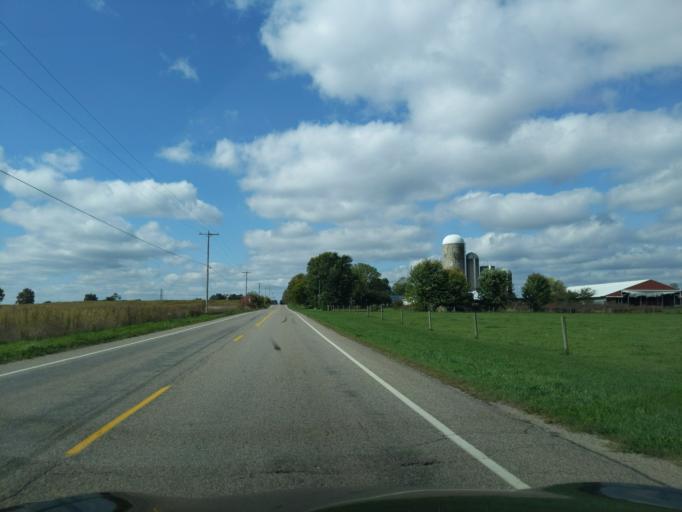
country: US
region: Michigan
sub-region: Eaton County
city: Potterville
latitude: 42.5676
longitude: -84.7589
